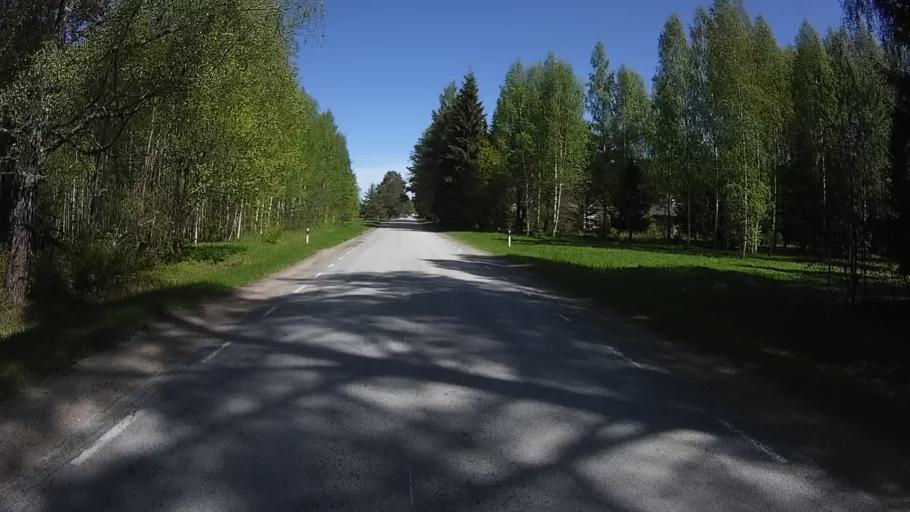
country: EE
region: Polvamaa
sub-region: Raepina vald
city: Rapina
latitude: 58.0828
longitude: 27.4340
